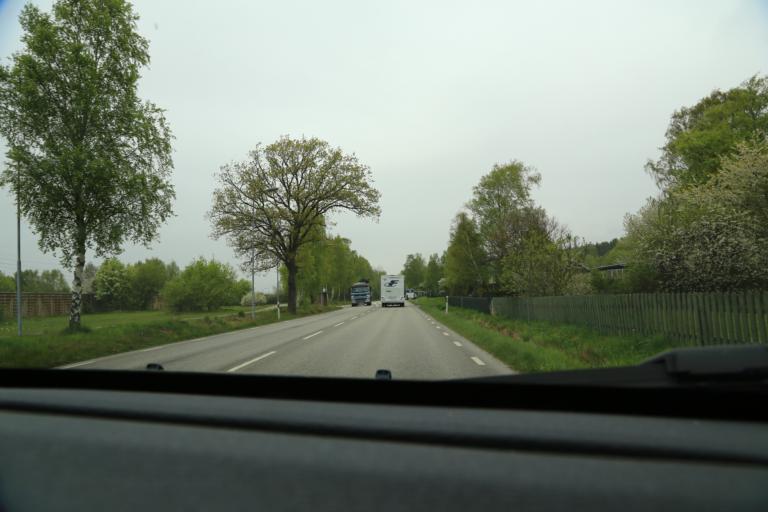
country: SE
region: Halland
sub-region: Varbergs Kommun
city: Varberg
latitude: 57.1730
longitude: 12.2288
